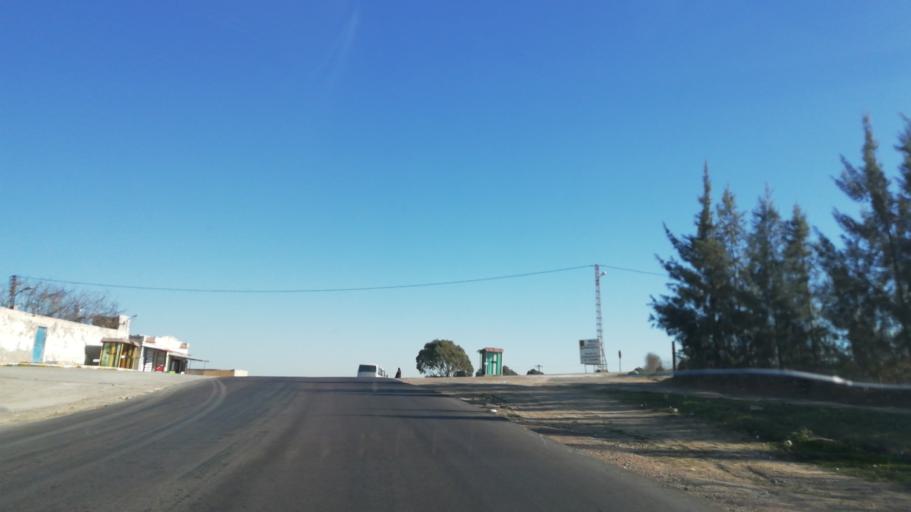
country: DZ
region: Relizane
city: Smala
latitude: 35.6752
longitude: 0.8008
